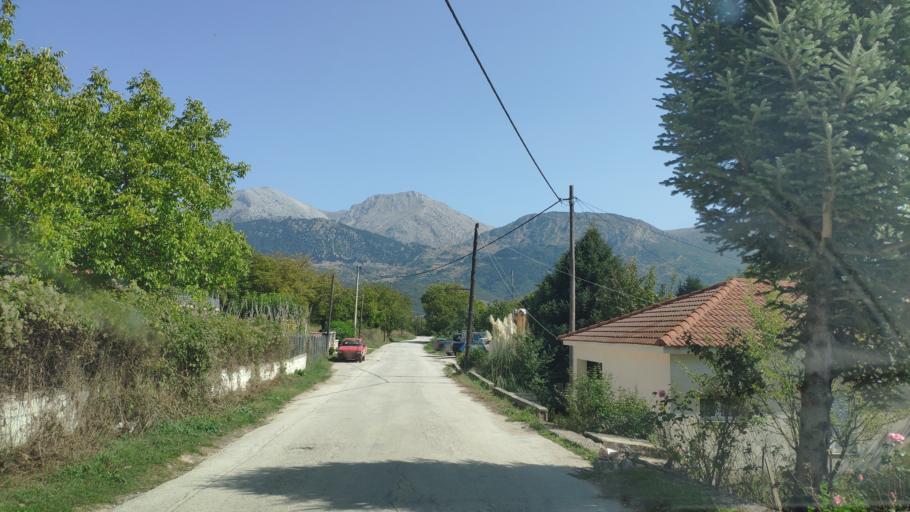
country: GR
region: West Greece
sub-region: Nomos Achaias
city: Kalavryta
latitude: 37.9128
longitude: 22.3019
